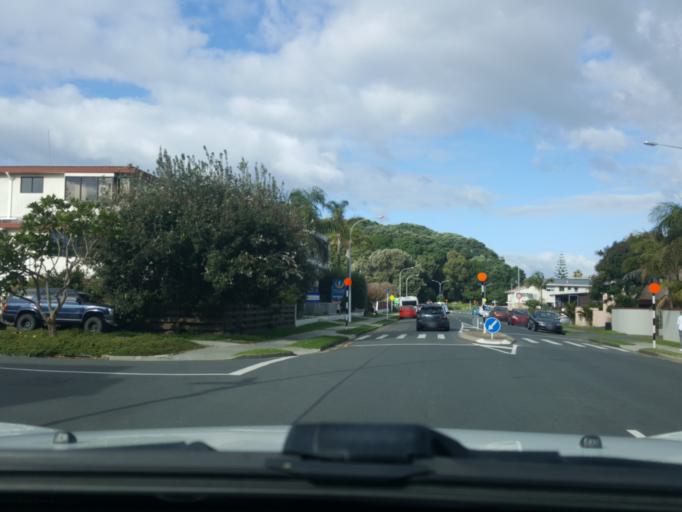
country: NZ
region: Bay of Plenty
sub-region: Tauranga City
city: Tauranga
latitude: -37.6339
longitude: 176.1798
